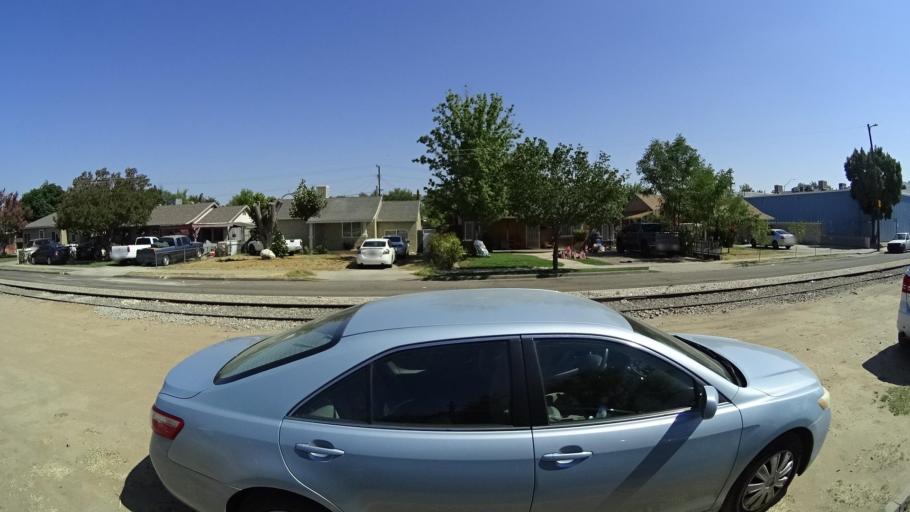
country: US
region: California
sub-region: Fresno County
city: Fresno
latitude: 36.7614
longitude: -119.7735
